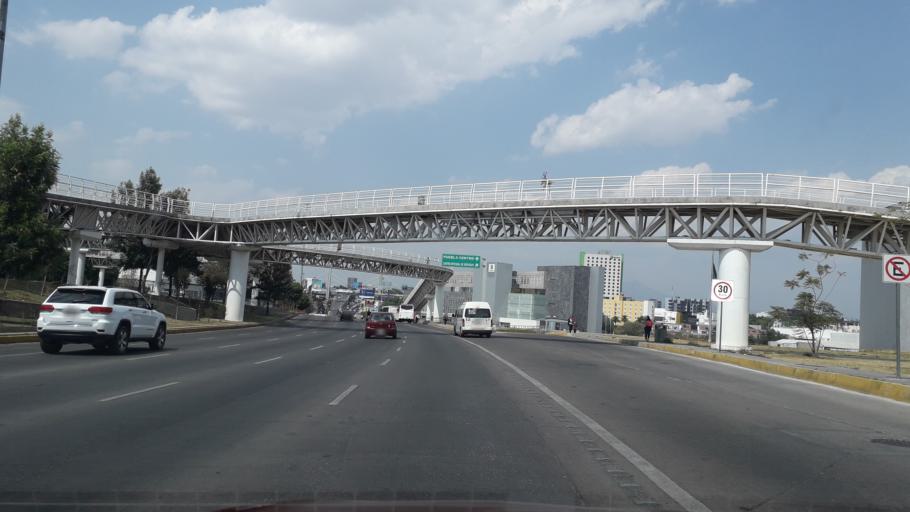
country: MX
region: Puebla
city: Puebla
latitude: 19.0311
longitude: -98.2290
